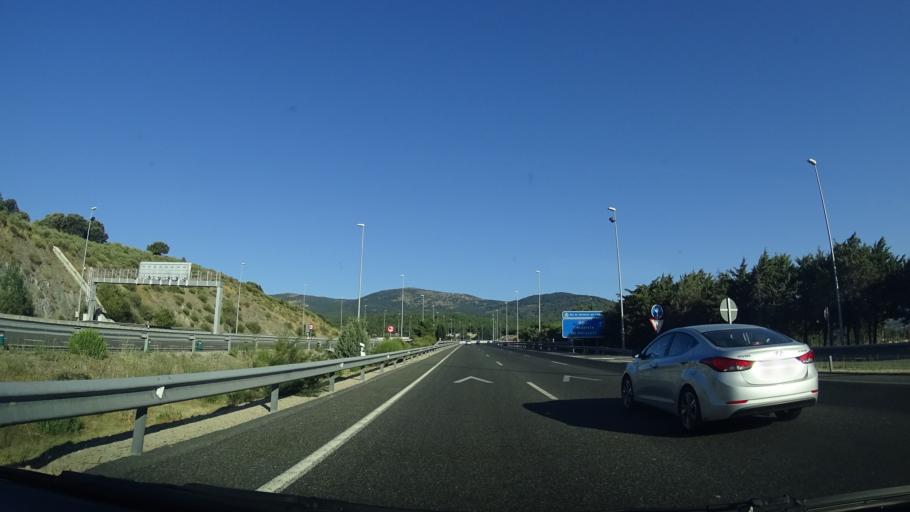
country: ES
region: Madrid
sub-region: Provincia de Madrid
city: Guadarrama
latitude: 40.6697
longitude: -4.1065
